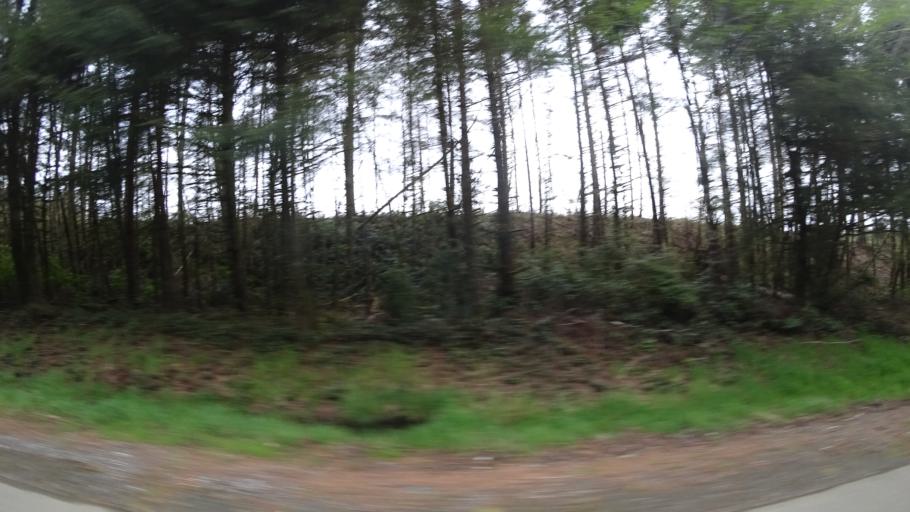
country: US
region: Oregon
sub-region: Coos County
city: Coquille
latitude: 43.2226
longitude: -124.3024
